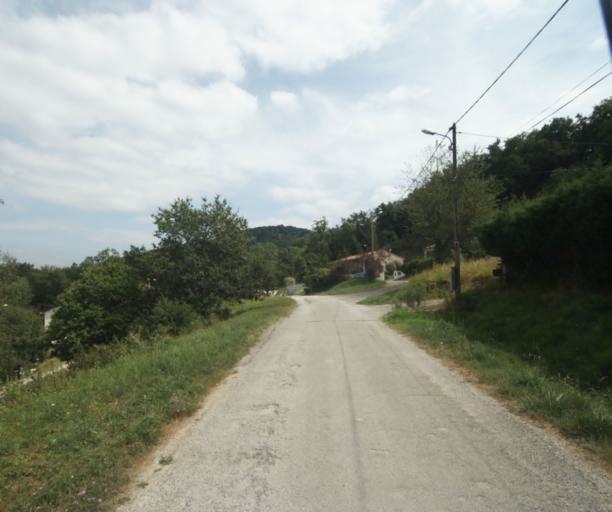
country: FR
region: Midi-Pyrenees
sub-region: Departement du Tarn
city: Soreze
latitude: 43.4376
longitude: 2.0446
